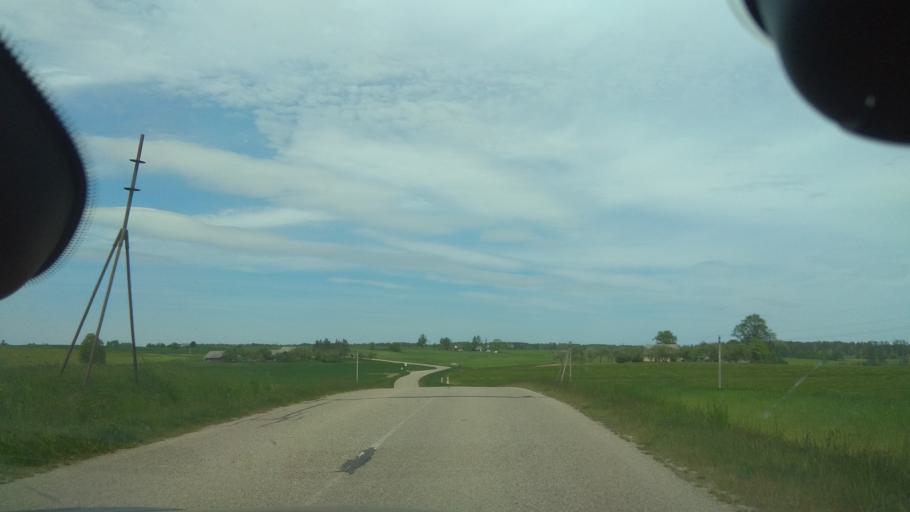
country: LT
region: Vilnius County
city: Ukmerge
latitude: 55.1576
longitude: 24.5437
